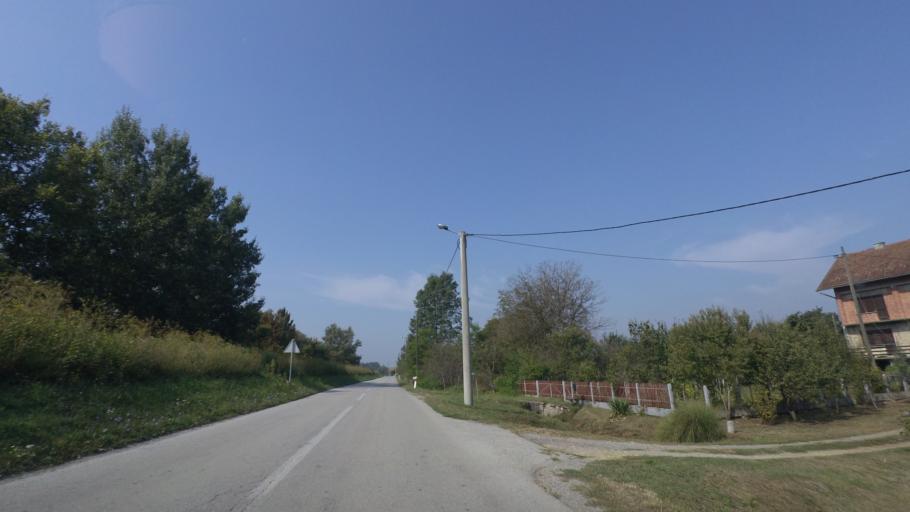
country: BA
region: Republika Srpska
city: Bosanska Dubica
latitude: 45.2404
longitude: 16.8661
